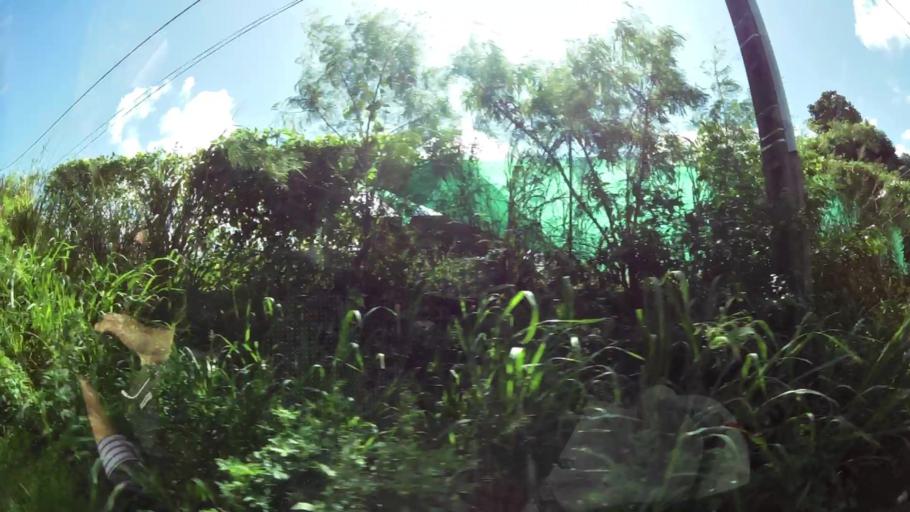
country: GP
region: Guadeloupe
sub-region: Guadeloupe
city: Petit-Canal
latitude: 16.3701
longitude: -61.4468
